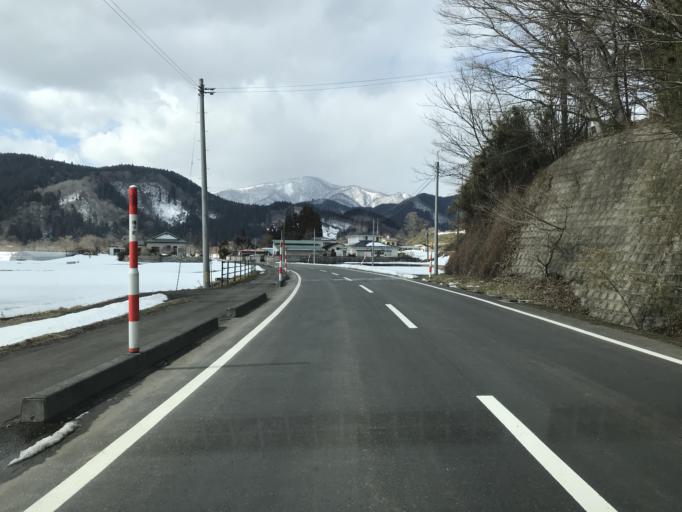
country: JP
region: Miyagi
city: Furukawa
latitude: 38.7430
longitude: 140.7458
